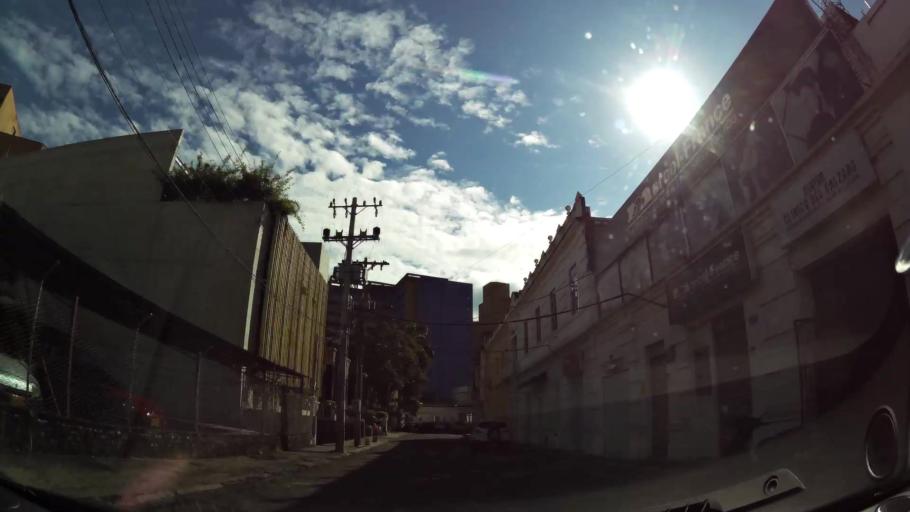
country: CO
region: Valle del Cauca
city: Cali
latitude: 3.4564
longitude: -76.5345
